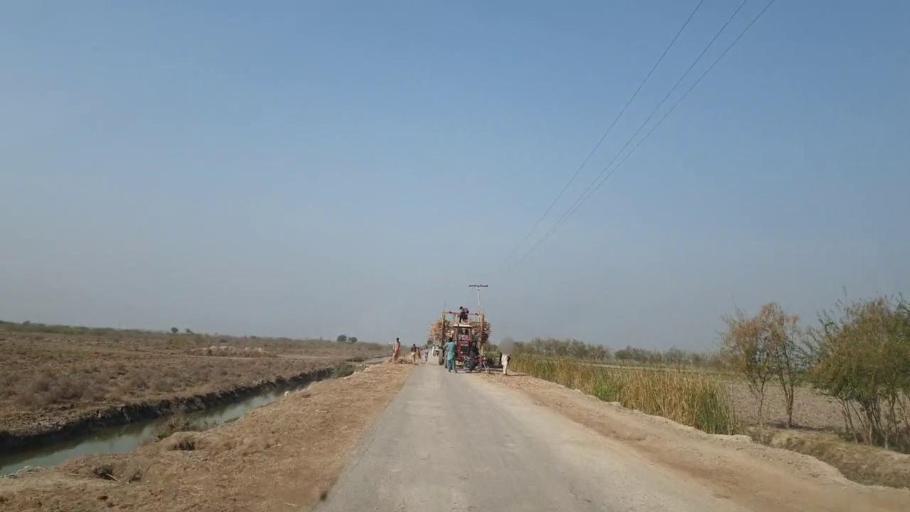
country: PK
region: Sindh
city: Mirpur Khas
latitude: 25.5828
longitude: 69.0378
